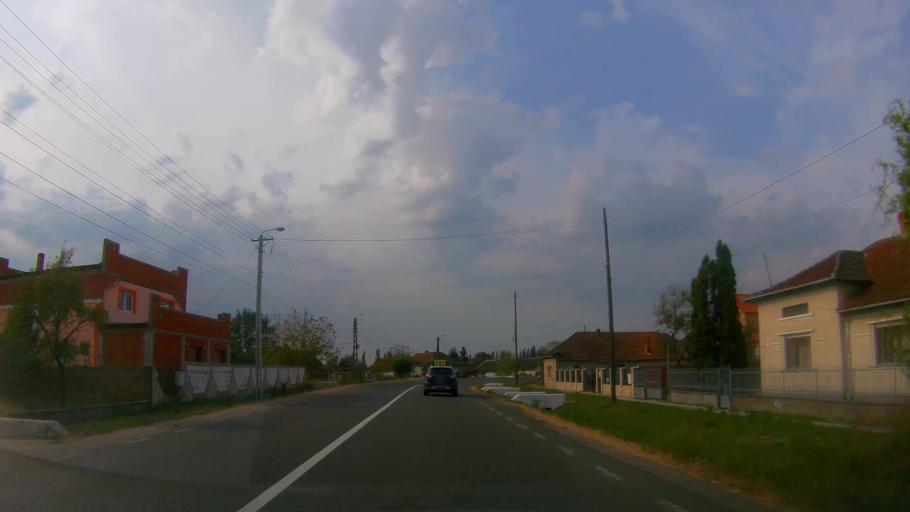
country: RO
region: Satu Mare
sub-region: Oras Ardud
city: Ardud
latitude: 47.6331
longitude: 22.8847
